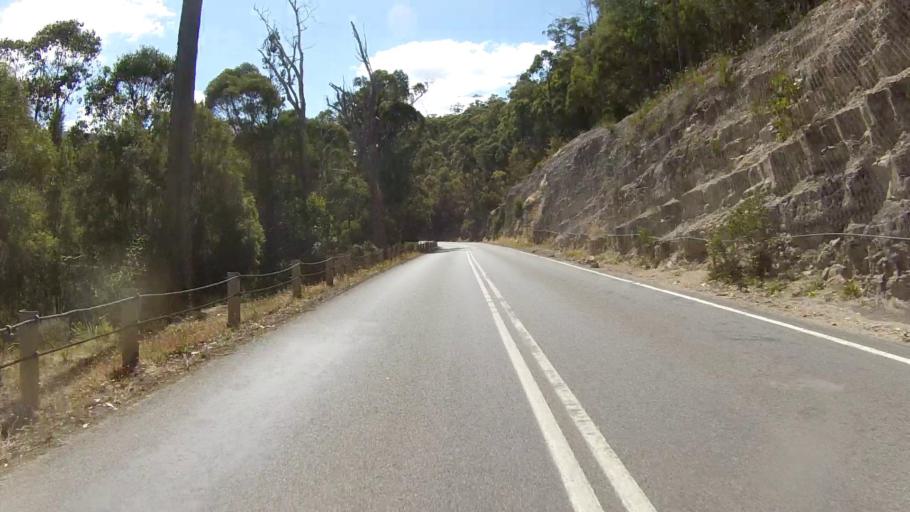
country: AU
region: Tasmania
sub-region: Derwent Valley
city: New Norfolk
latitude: -42.6858
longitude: 146.7259
